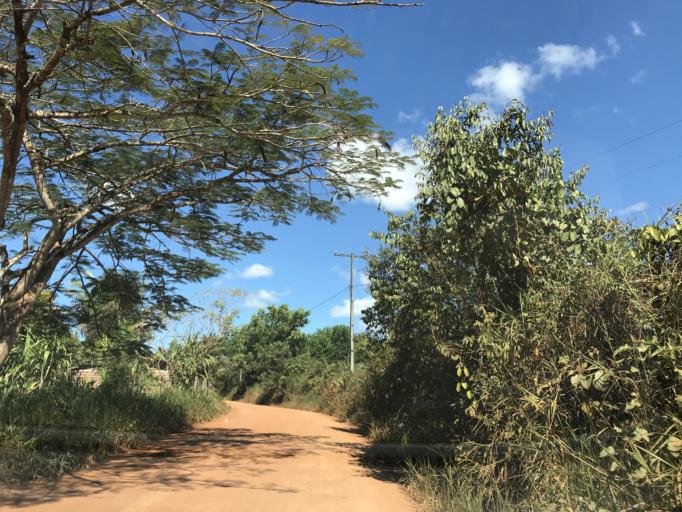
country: BR
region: Bahia
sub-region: Valenca
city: Valenca
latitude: -13.3184
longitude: -39.2402
